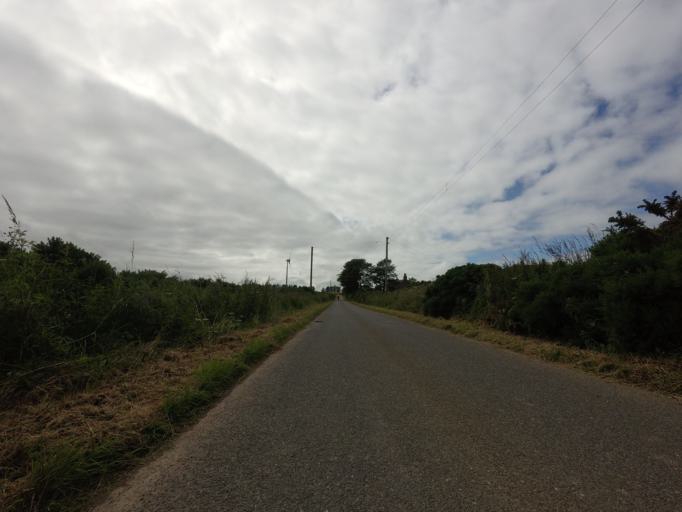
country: GB
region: Scotland
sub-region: Aberdeenshire
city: Turriff
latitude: 57.5453
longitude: -2.2868
